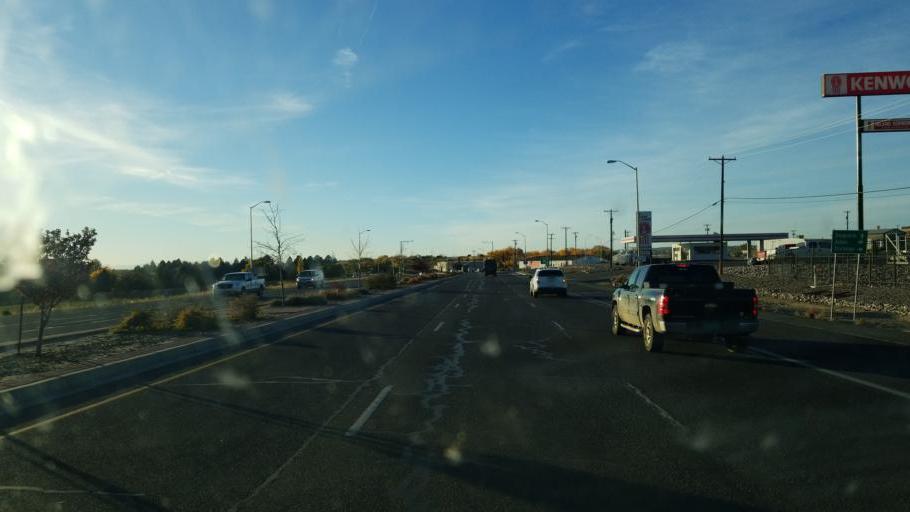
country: US
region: New Mexico
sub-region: San Juan County
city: Farmington
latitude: 36.7177
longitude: -108.1551
